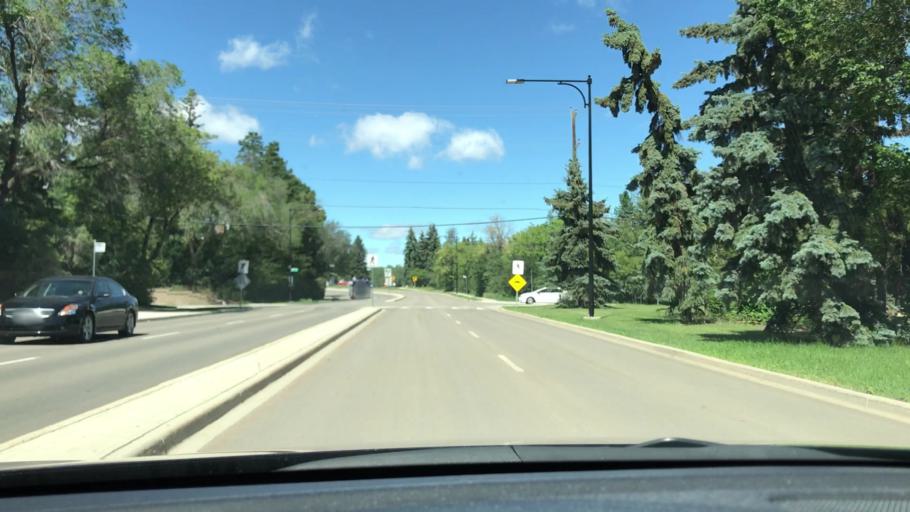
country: CA
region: Alberta
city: Edmonton
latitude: 53.5145
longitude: -113.5560
